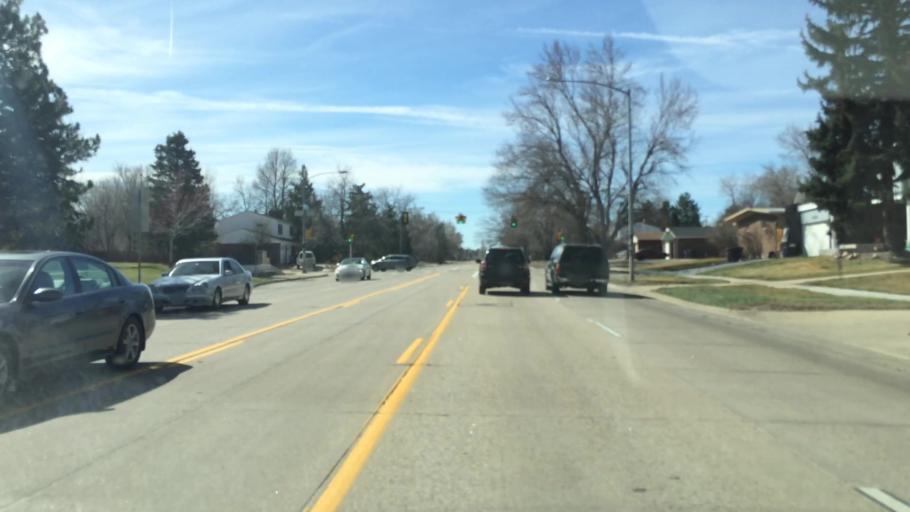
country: US
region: Colorado
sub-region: Arapahoe County
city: Glendale
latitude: 39.6865
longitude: -104.9129
